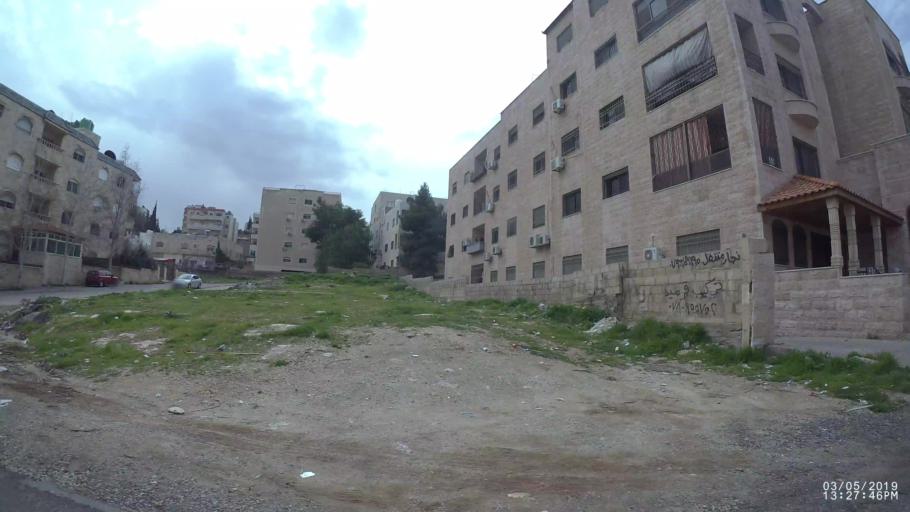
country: JO
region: Amman
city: Amman
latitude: 32.0011
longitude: 35.9362
